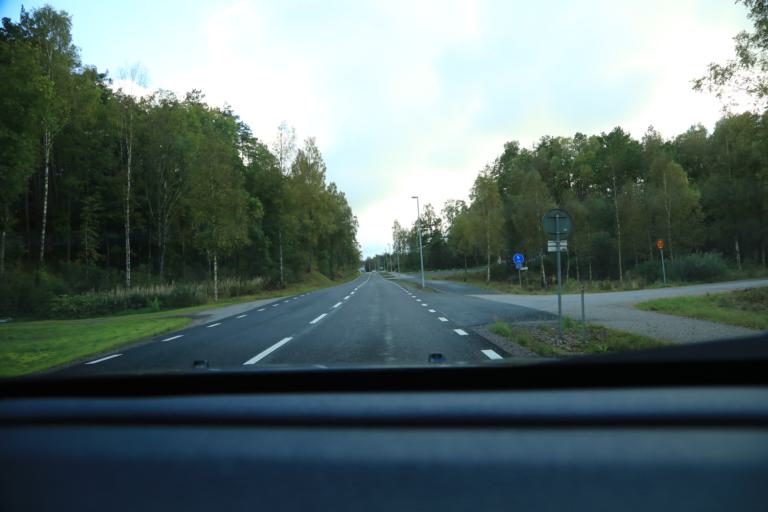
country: SE
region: Halland
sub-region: Halmstads Kommun
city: Getinge
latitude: 57.1324
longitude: 12.7178
